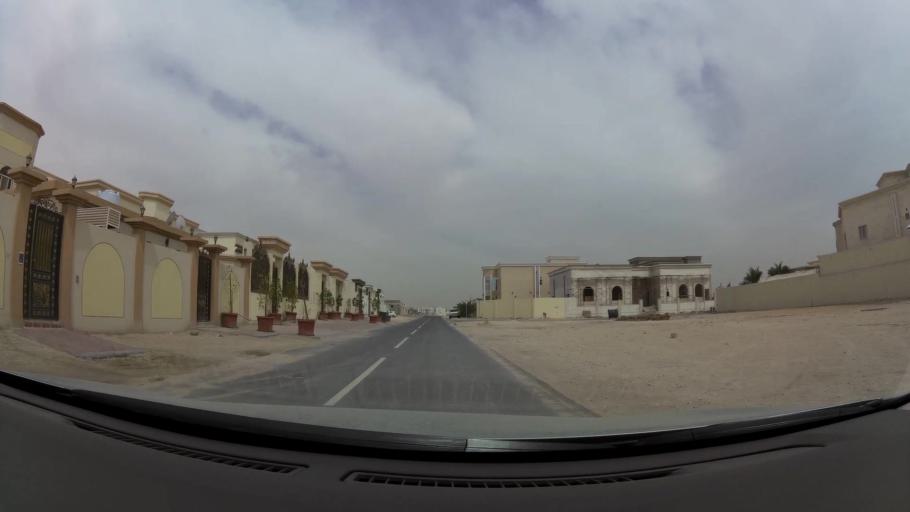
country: QA
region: Baladiyat ad Dawhah
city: Doha
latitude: 25.2098
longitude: 51.4662
